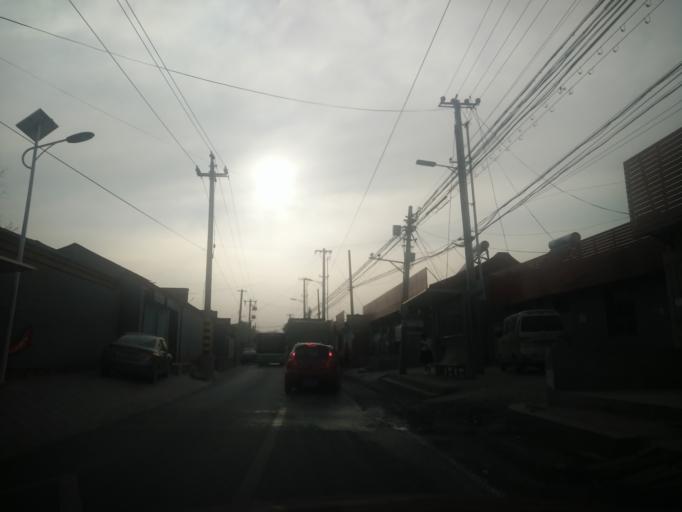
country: CN
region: Beijing
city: Qingyundian
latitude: 39.6791
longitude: 116.4775
